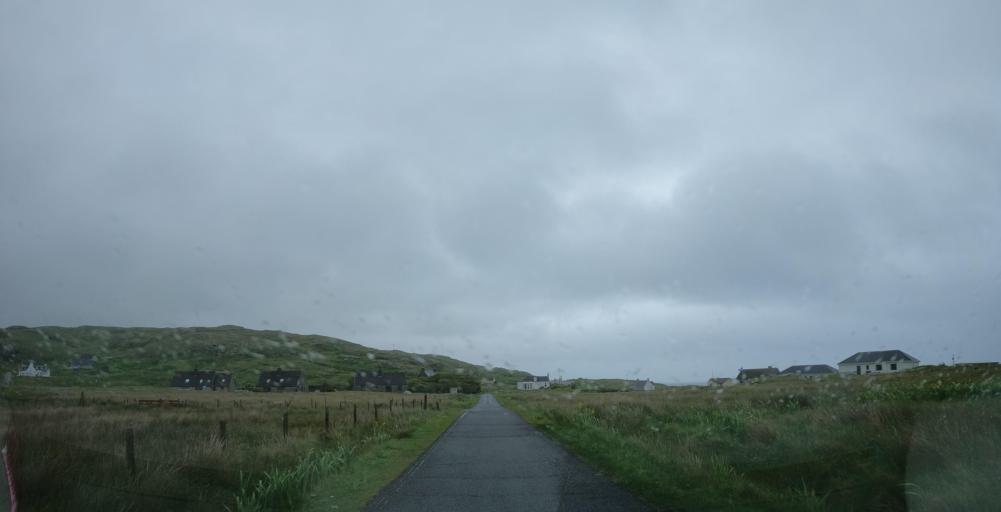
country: GB
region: Scotland
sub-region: Eilean Siar
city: Barra
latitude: 56.9656
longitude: -7.4347
